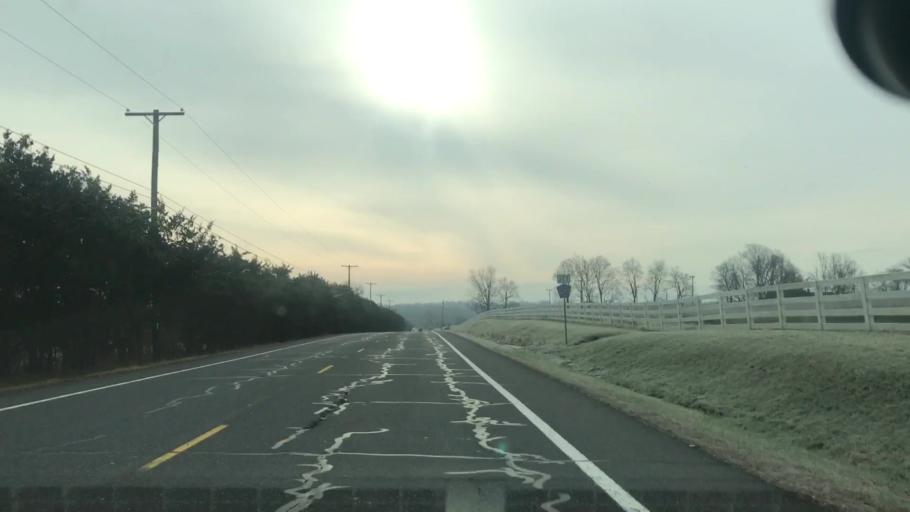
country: US
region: New Jersey
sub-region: Hunterdon County
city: Whitehouse Station
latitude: 40.6306
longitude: -74.7081
